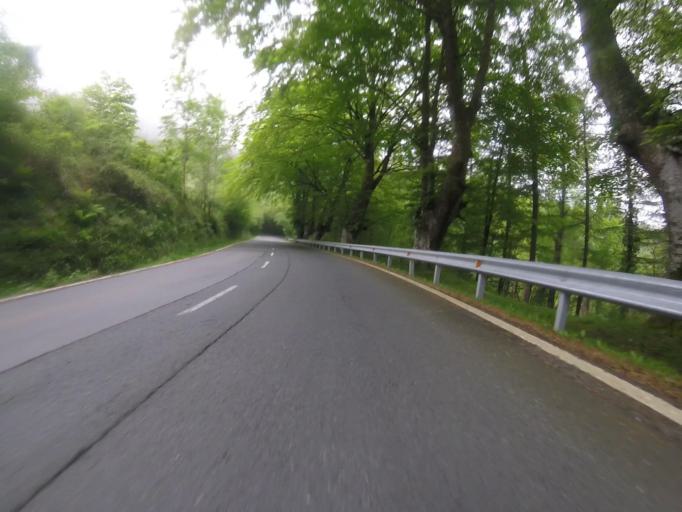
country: ES
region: Navarre
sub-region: Provincia de Navarra
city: Zugarramurdi
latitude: 43.2429
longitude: -1.4819
